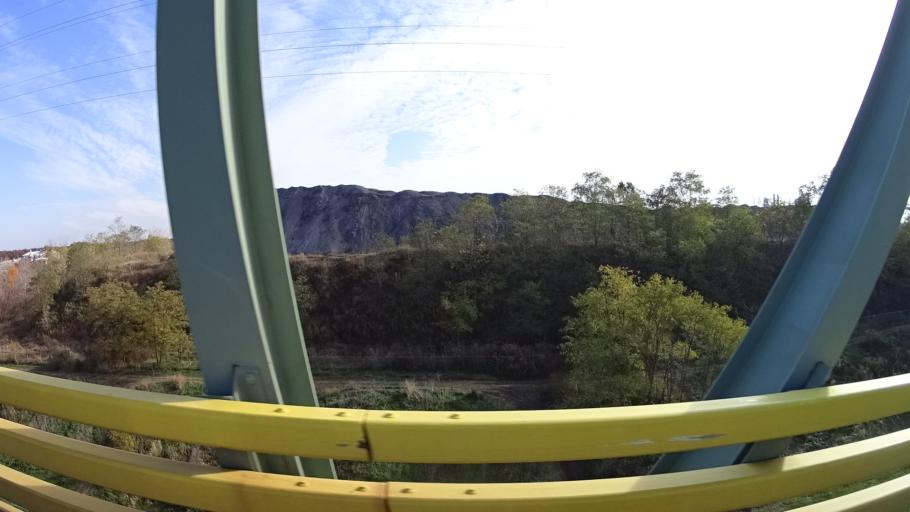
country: US
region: Ohio
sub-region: Lorain County
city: Lorain
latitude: 41.4554
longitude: -82.1603
